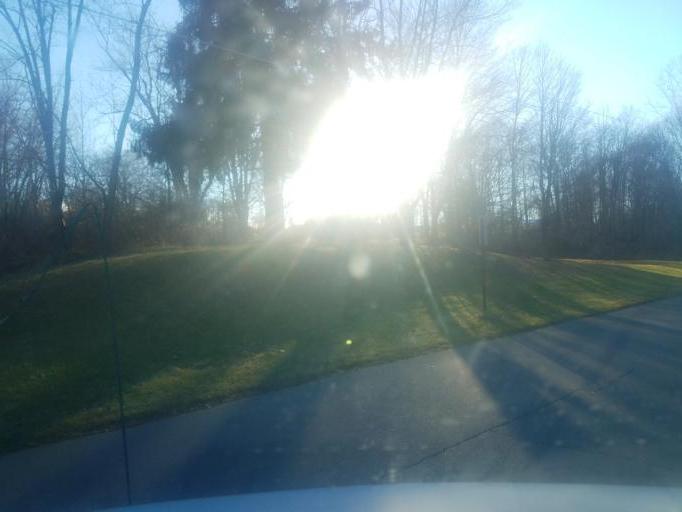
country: US
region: Ohio
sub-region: Richland County
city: Mansfield
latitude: 40.7894
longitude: -82.5341
